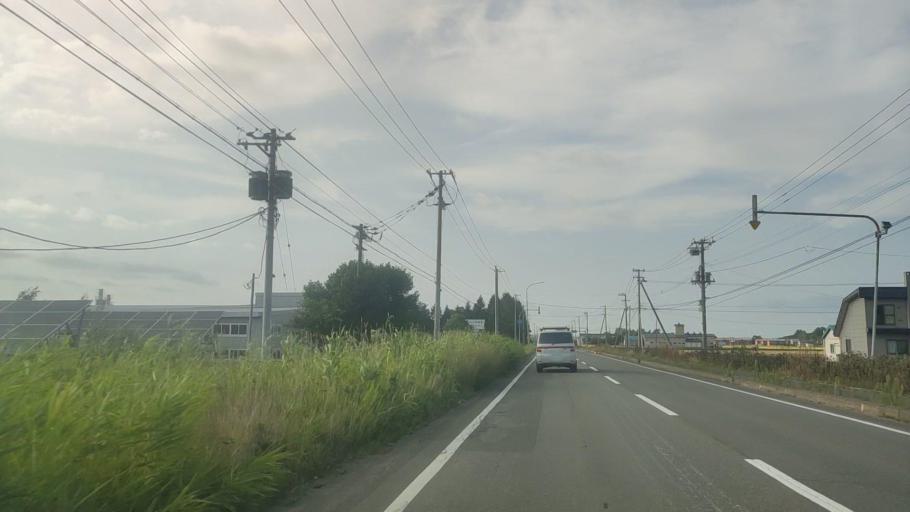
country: JP
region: Hokkaido
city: Chitose
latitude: 42.9326
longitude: 141.8064
